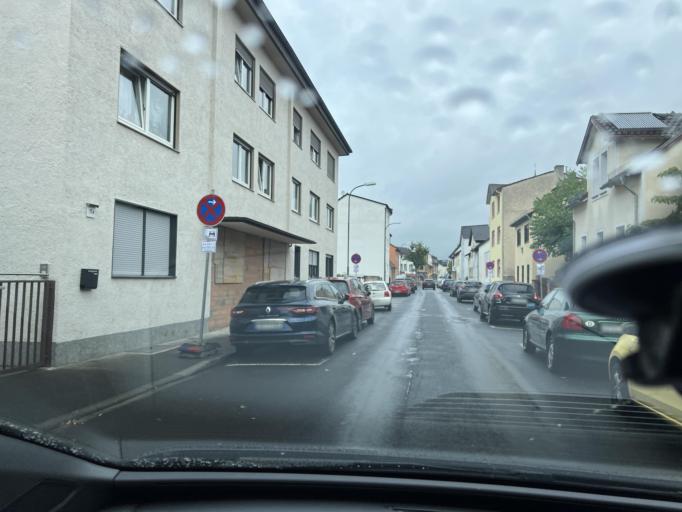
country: DE
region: Hesse
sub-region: Regierungsbezirk Darmstadt
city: Offenbach
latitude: 50.1139
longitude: 8.7843
